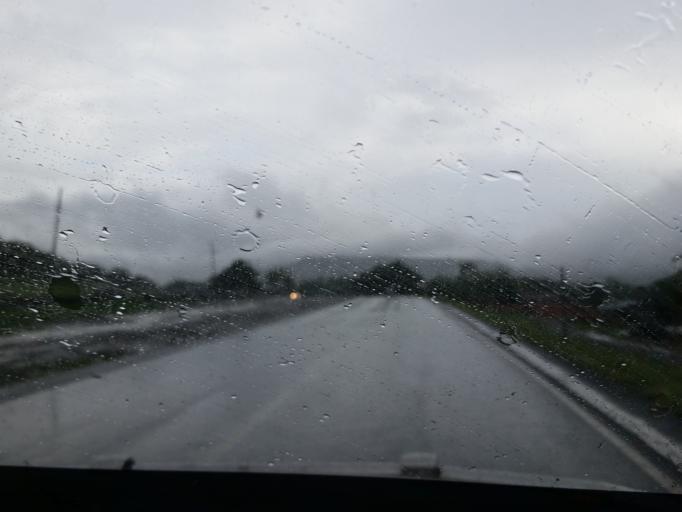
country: NI
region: Matagalpa
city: Ciudad Dario
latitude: 12.6738
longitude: -86.0882
